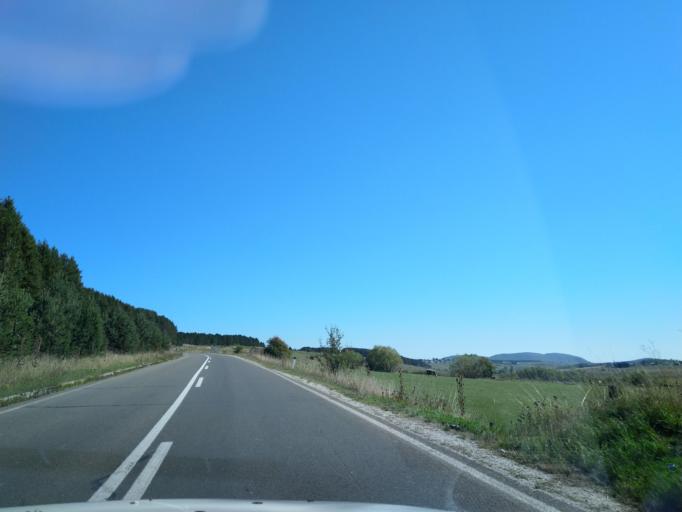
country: RS
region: Central Serbia
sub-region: Zlatiborski Okrug
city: Sjenica
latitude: 43.2683
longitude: 20.0282
